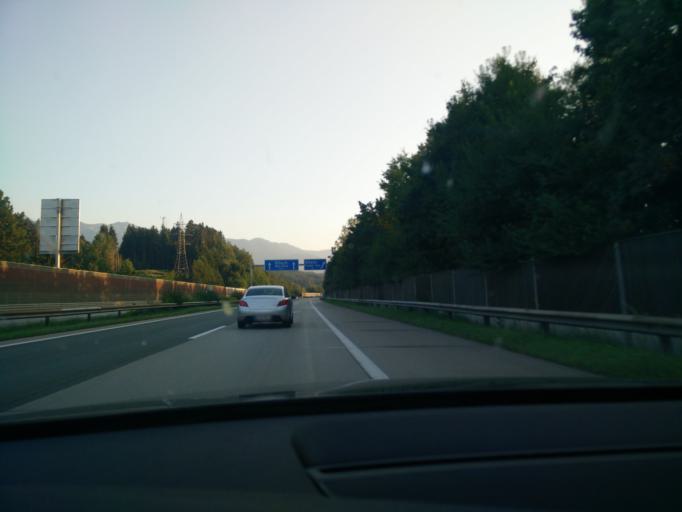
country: AT
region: Carinthia
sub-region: Villach Stadt
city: Villach
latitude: 46.6044
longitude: 13.8890
